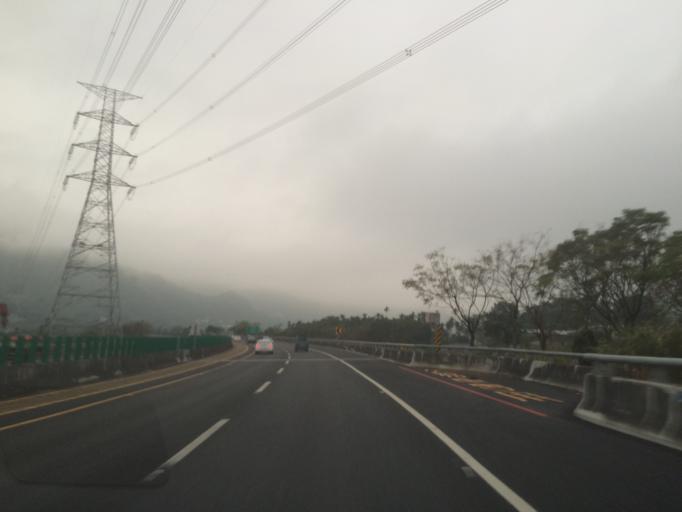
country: TW
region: Taiwan
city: Zhongxing New Village
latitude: 23.9974
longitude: 120.8019
